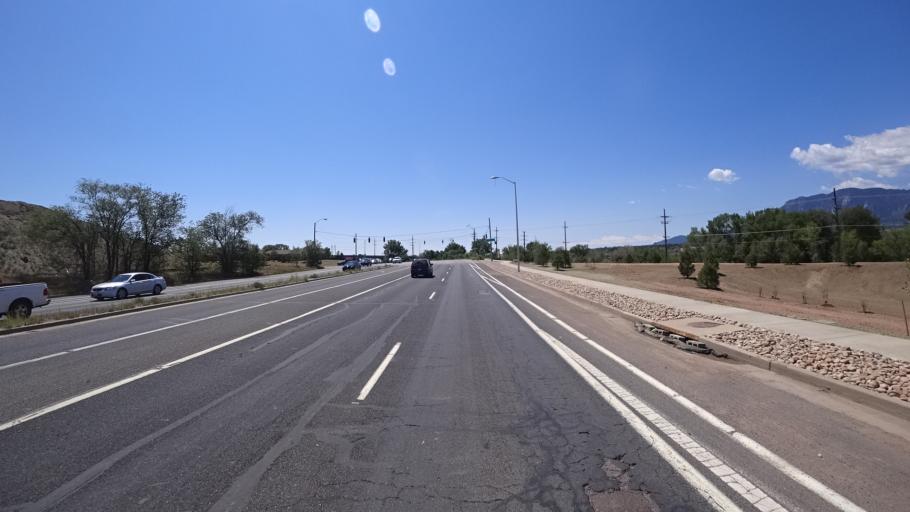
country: US
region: Colorado
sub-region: El Paso County
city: Stratmoor
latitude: 38.8007
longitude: -104.7854
